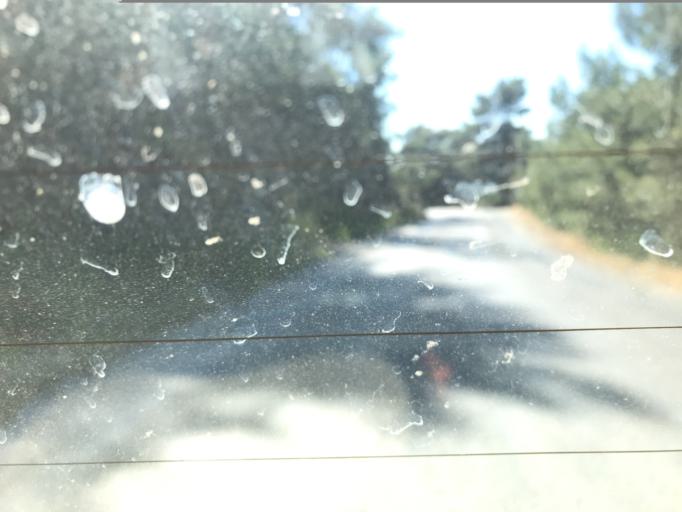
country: TR
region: Mugla
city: Selimiye
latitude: 37.3889
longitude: 27.4728
